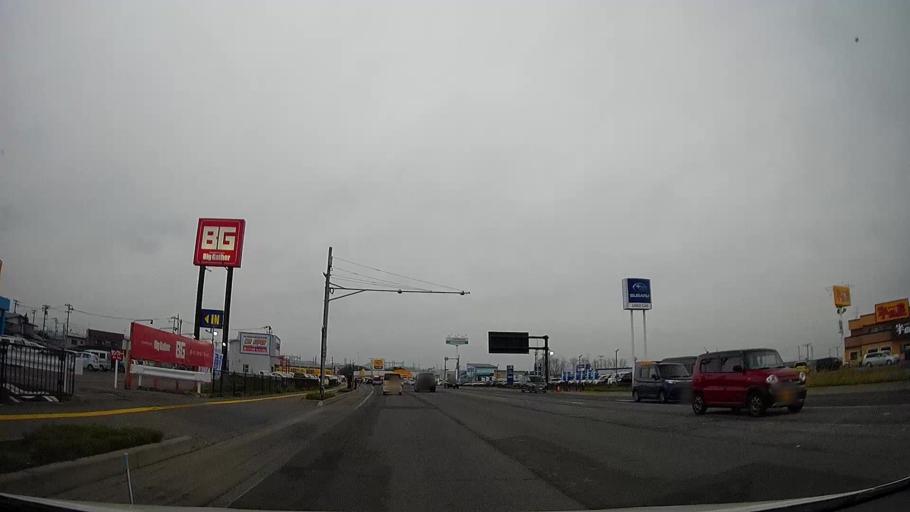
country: JP
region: Aomori
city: Aomori Shi
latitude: 40.8325
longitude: 140.7006
